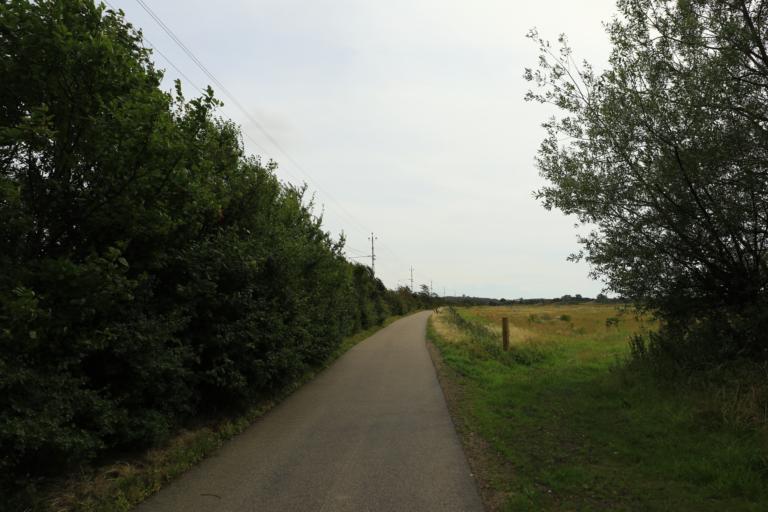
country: SE
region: Halland
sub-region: Varbergs Kommun
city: Varberg
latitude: 57.1397
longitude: 12.2587
